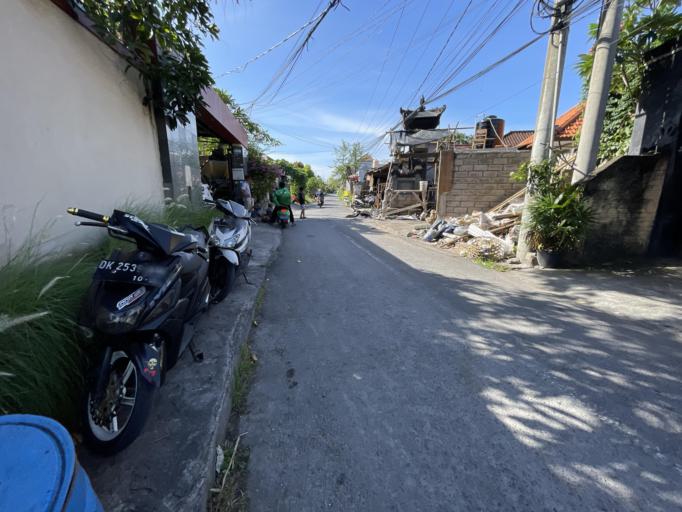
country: ID
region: Bali
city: Kuta
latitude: -8.6762
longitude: 115.1695
